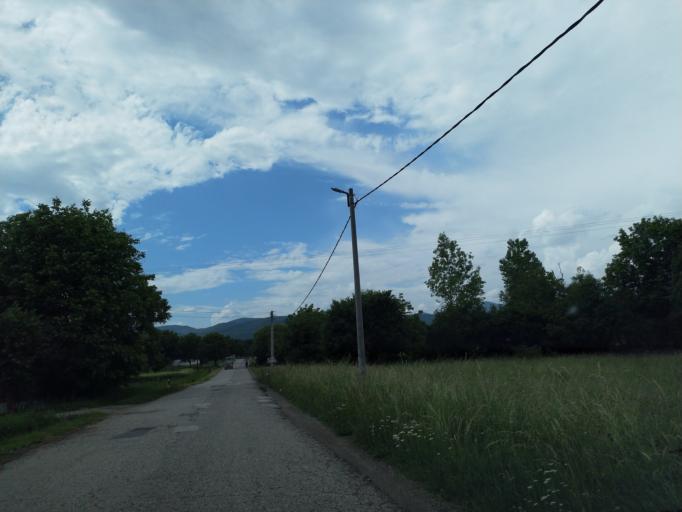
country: RS
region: Central Serbia
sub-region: Zajecarski Okrug
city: Boljevac
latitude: 43.8940
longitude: 21.9647
